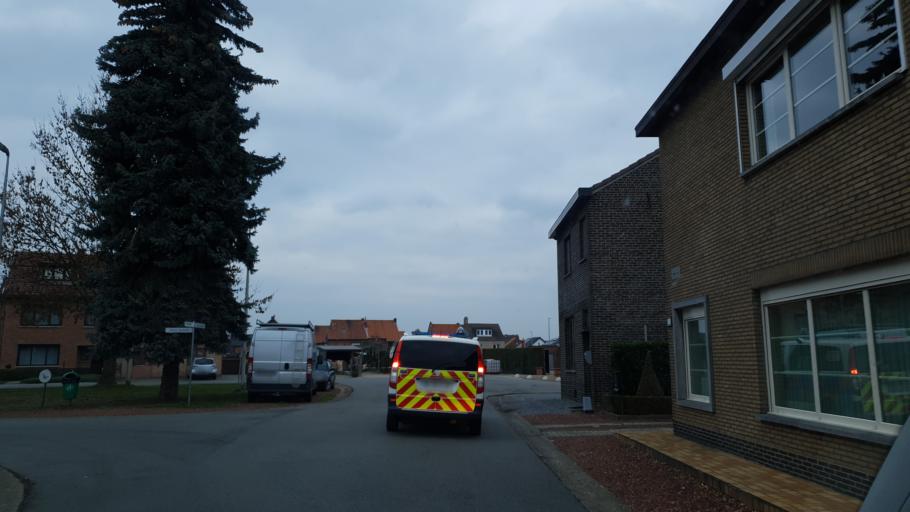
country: BE
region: Flanders
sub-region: Provincie Limburg
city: Lanaken
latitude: 50.8948
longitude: 5.6498
